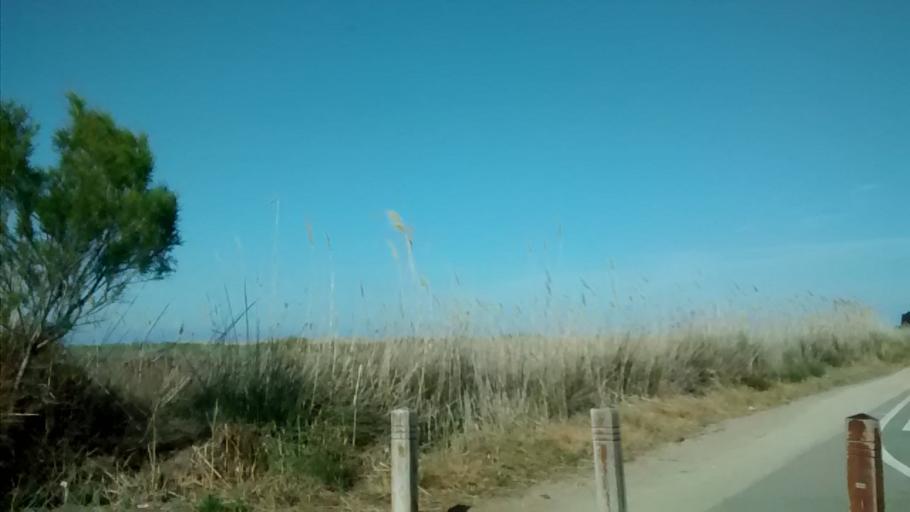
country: ES
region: Catalonia
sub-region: Provincia de Tarragona
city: Deltebre
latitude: 40.7197
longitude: 0.8558
